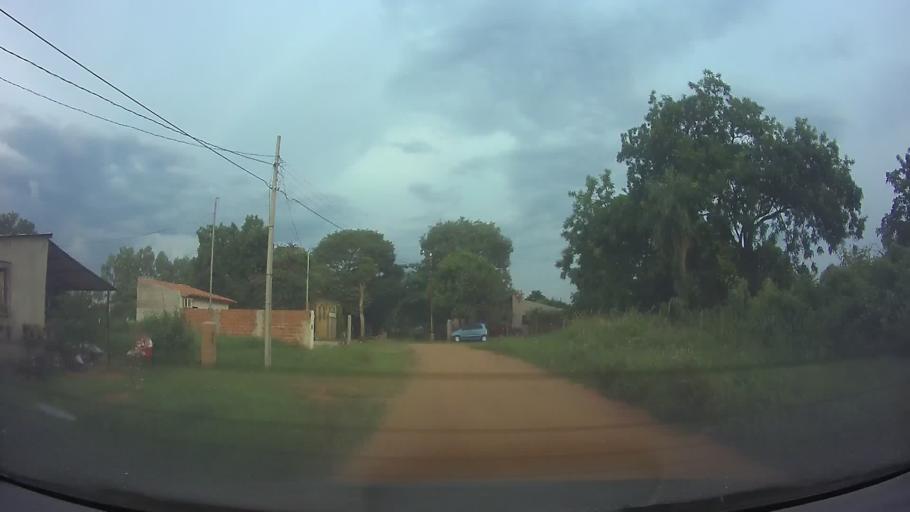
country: PY
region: Central
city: San Lorenzo
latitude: -25.2596
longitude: -57.4641
